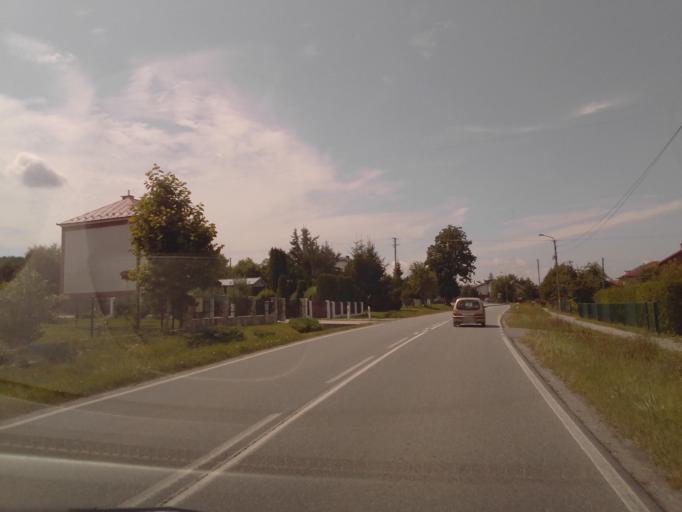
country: PL
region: Subcarpathian Voivodeship
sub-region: Powiat ropczycko-sedziszowski
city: Ropczyce
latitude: 50.0419
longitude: 21.5878
